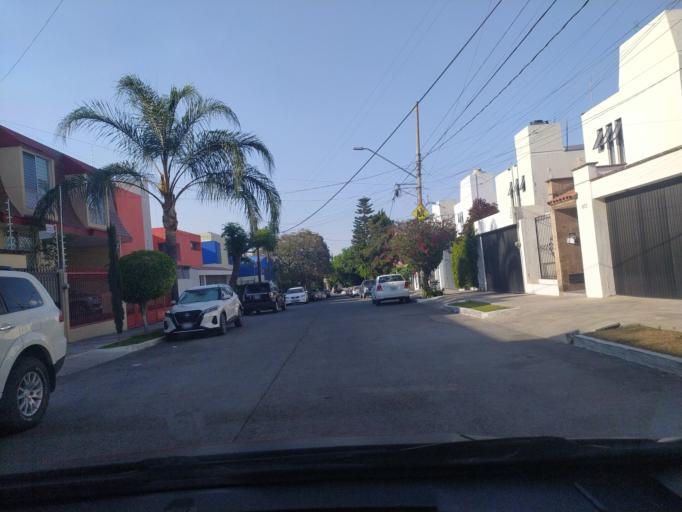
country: MX
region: Jalisco
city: Guadalajara
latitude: 20.6929
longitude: -103.3878
